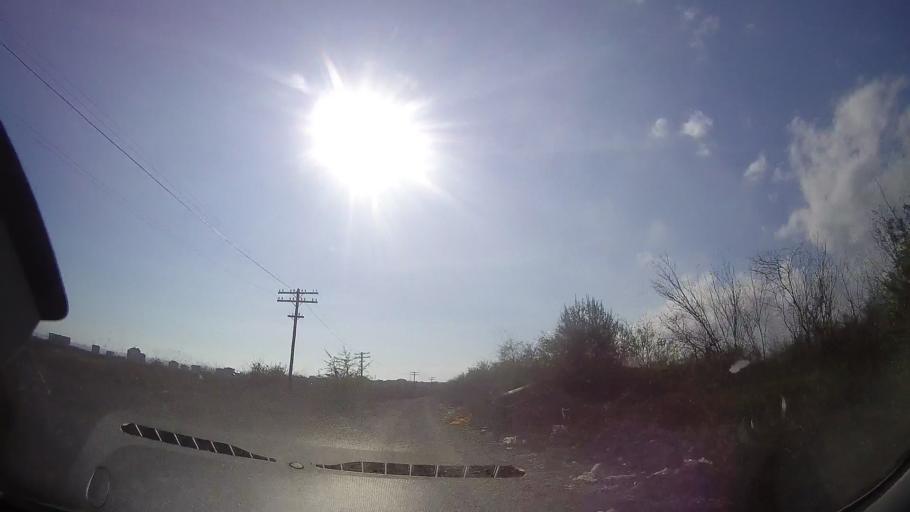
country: RO
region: Constanta
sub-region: Comuna Costinesti
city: Costinesti
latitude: 43.9698
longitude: 28.6424
